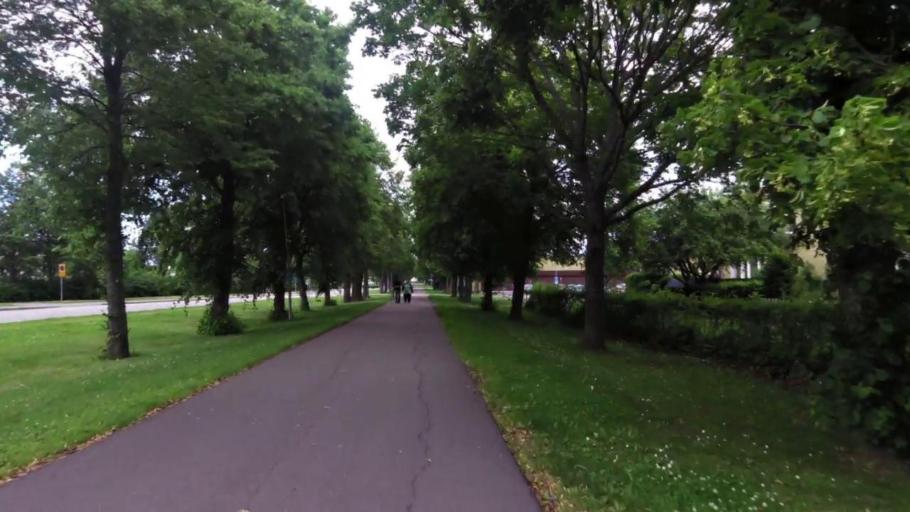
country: SE
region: OEstergoetland
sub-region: Linkopings Kommun
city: Malmslatt
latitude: 58.4070
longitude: 15.5660
